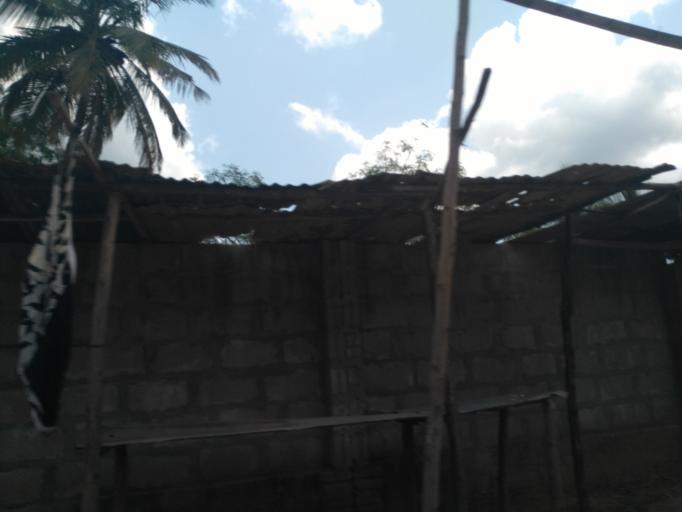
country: TZ
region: Dar es Salaam
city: Dar es Salaam
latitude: -6.8498
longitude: 39.3559
